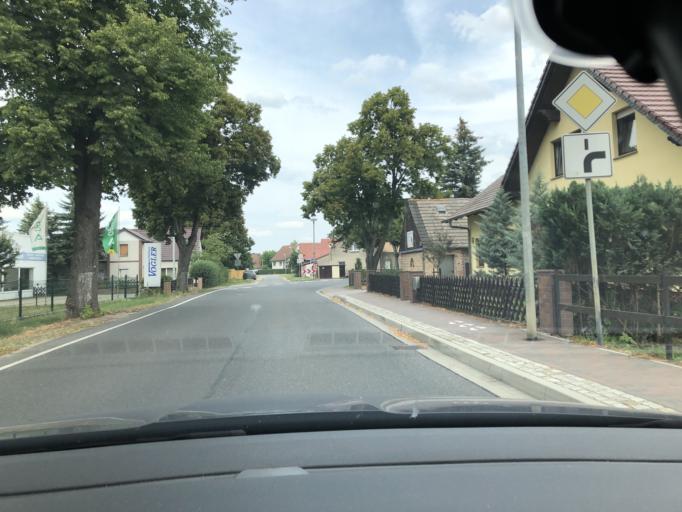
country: DE
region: Brandenburg
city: Kasel-Golzig
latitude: 51.9804
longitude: 13.7662
